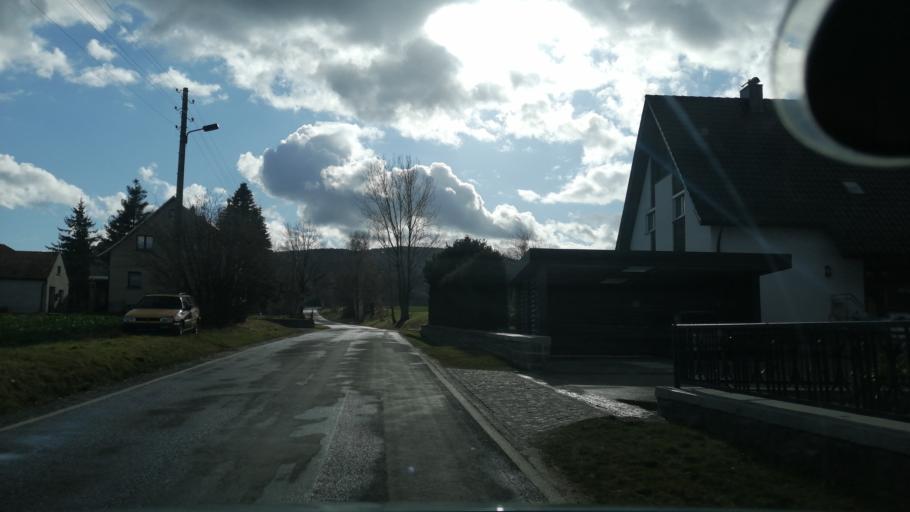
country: DE
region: Saxony
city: Kubschutz
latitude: 51.1429
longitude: 14.5353
